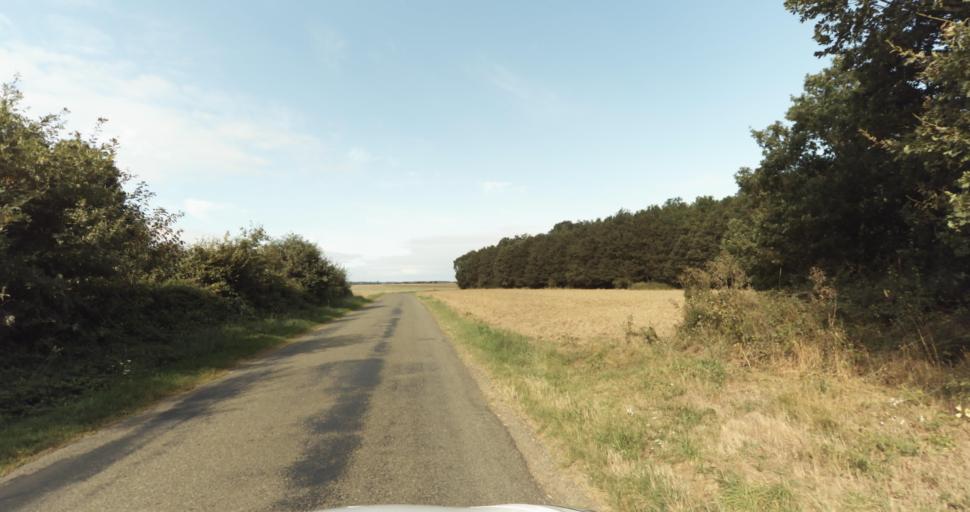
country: FR
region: Haute-Normandie
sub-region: Departement de l'Eure
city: Nonancourt
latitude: 48.8216
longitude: 1.1659
